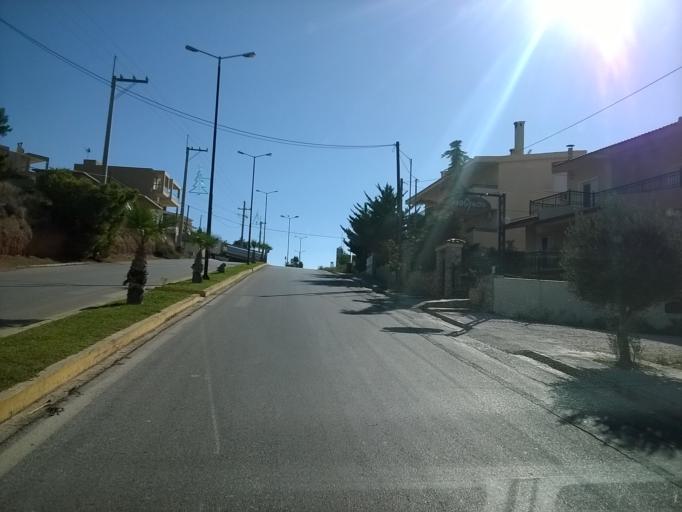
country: GR
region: Attica
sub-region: Nomarchia Anatolikis Attikis
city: Saronida
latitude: 37.7441
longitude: 23.9217
